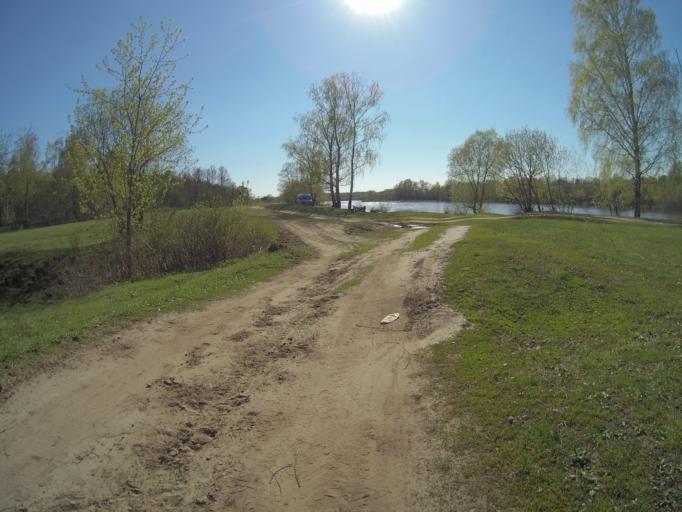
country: RU
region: Vladimir
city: Sudogda
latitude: 56.1531
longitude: 40.8251
